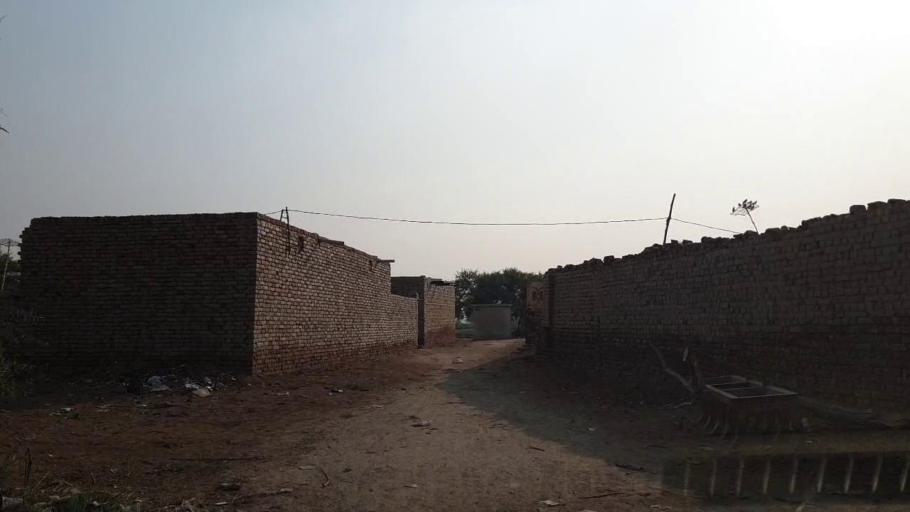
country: PK
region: Sindh
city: Bhan
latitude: 26.4725
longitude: 67.7262
